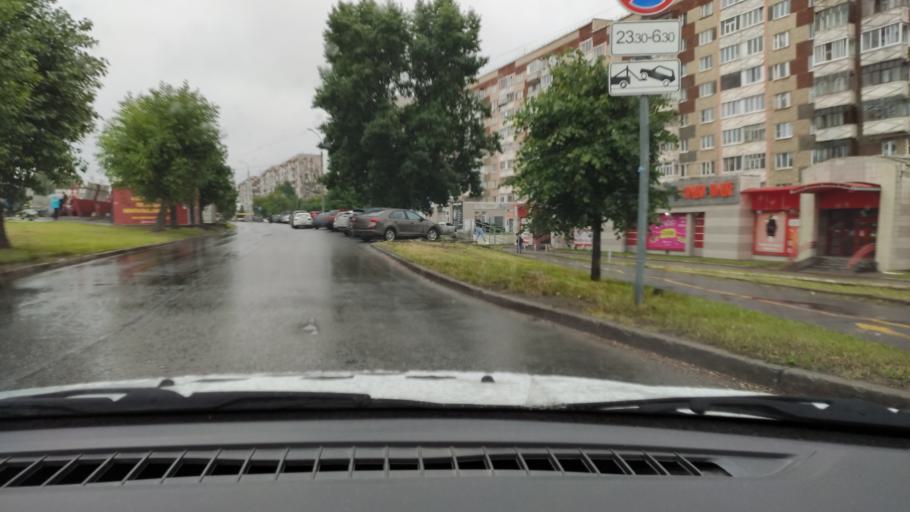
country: RU
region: Udmurtiya
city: Izhevsk
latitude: 56.8780
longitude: 53.2220
